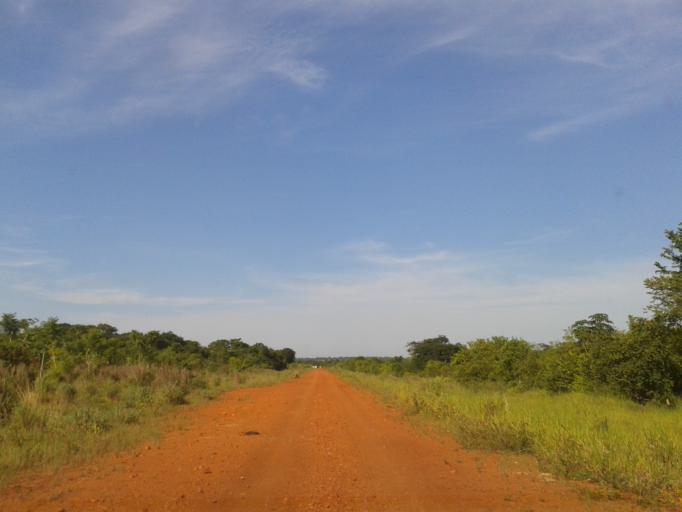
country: BR
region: Minas Gerais
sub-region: Santa Vitoria
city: Santa Vitoria
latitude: -19.1148
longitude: -50.5459
